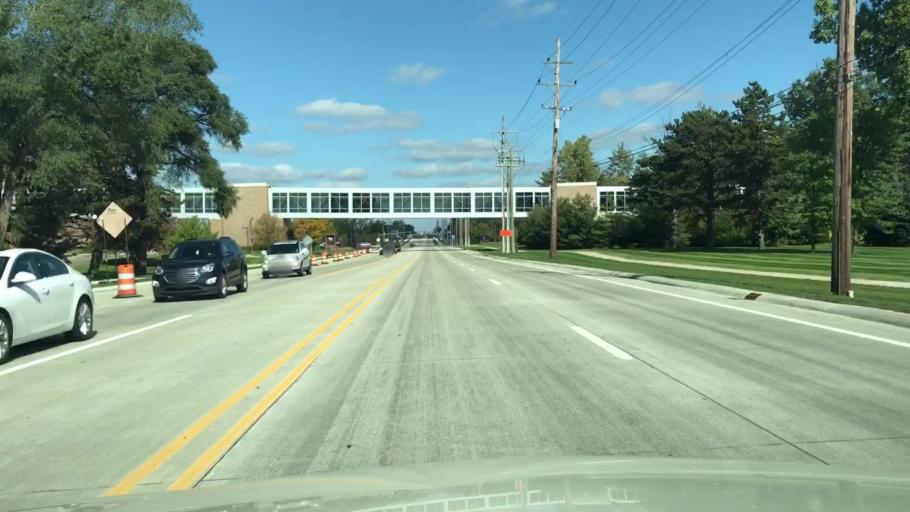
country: US
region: Michigan
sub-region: Macomb County
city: Utica
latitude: 42.6168
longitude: -83.0910
